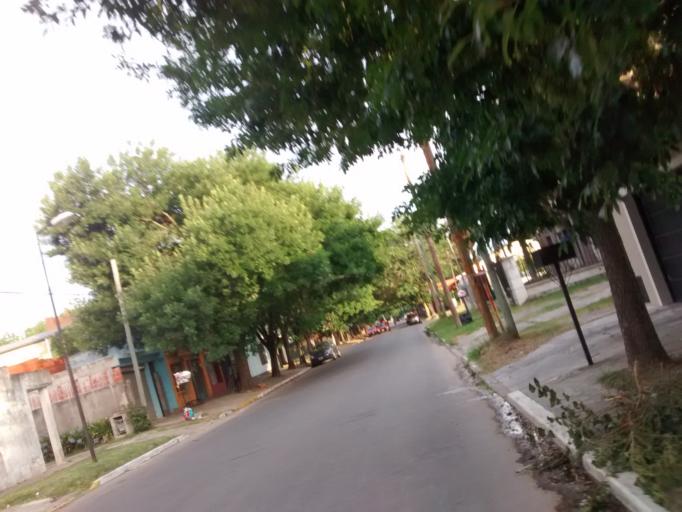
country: AR
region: Buenos Aires
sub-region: Partido de La Plata
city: La Plata
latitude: -34.8867
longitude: -58.0594
